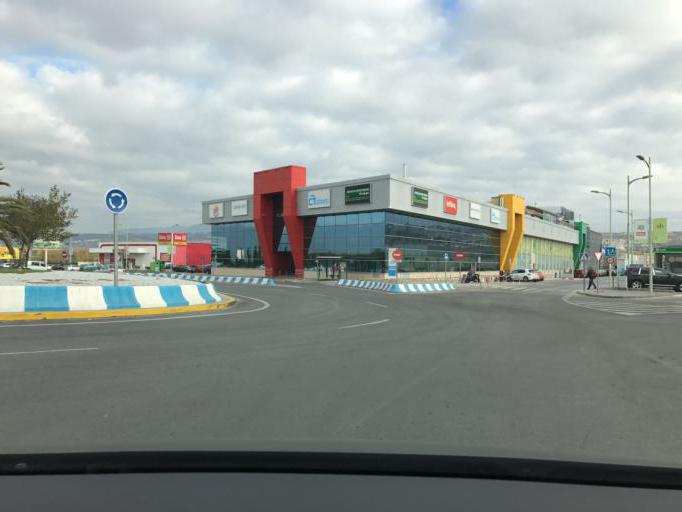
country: ES
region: Andalusia
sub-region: Provincia de Granada
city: Zubia
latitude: 37.1284
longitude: -3.5858
